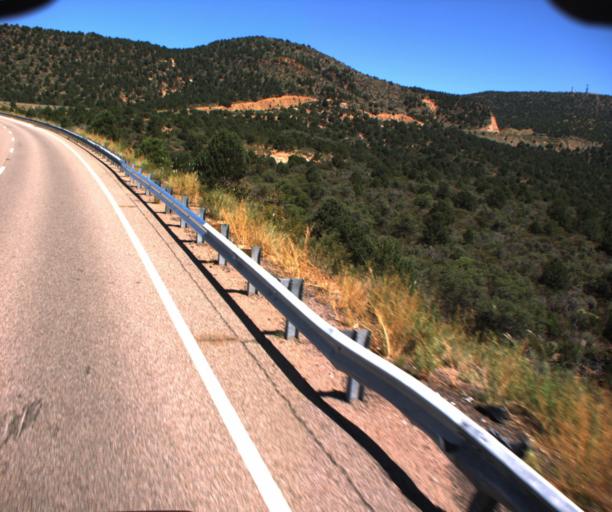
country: US
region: Arizona
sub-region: Gila County
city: San Carlos
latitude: 33.6436
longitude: -110.5749
